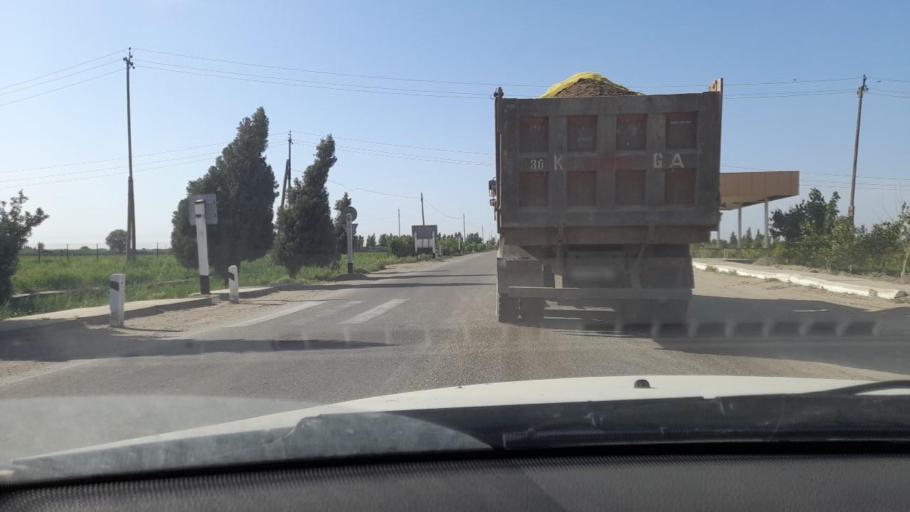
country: UZ
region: Bukhara
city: Romiton
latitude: 40.0452
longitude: 64.3289
